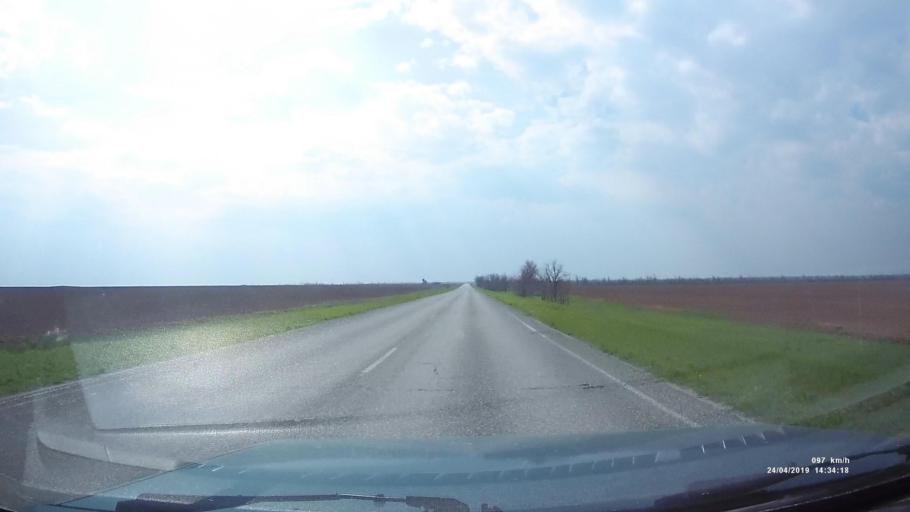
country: RU
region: Kalmykiya
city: Arshan'
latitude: 46.3737
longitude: 43.9346
